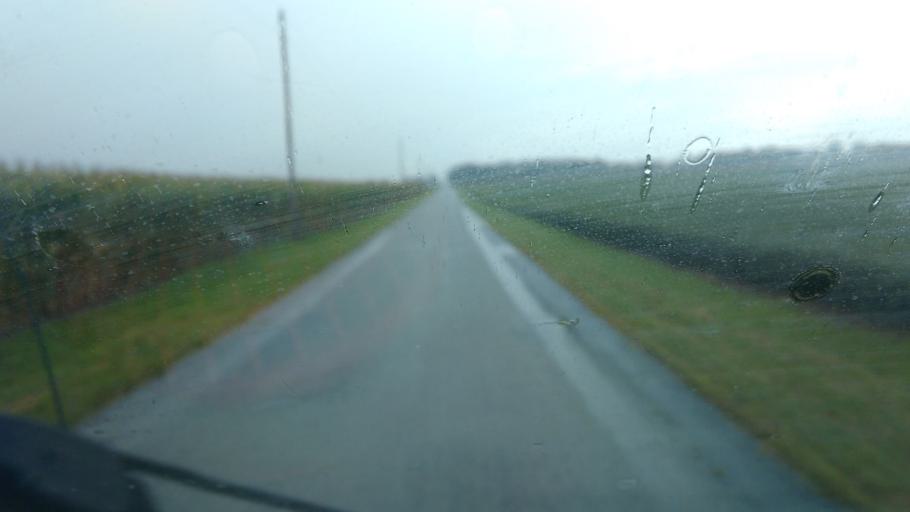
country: US
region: Ohio
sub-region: Hardin County
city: Kenton
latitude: 40.7169
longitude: -83.5682
